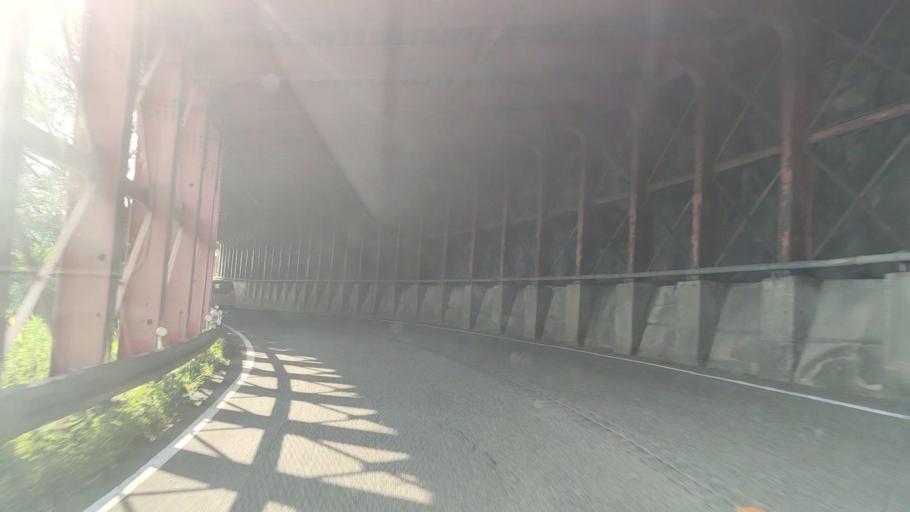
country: JP
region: Fukui
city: Takefu
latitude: 35.7905
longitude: 136.0961
